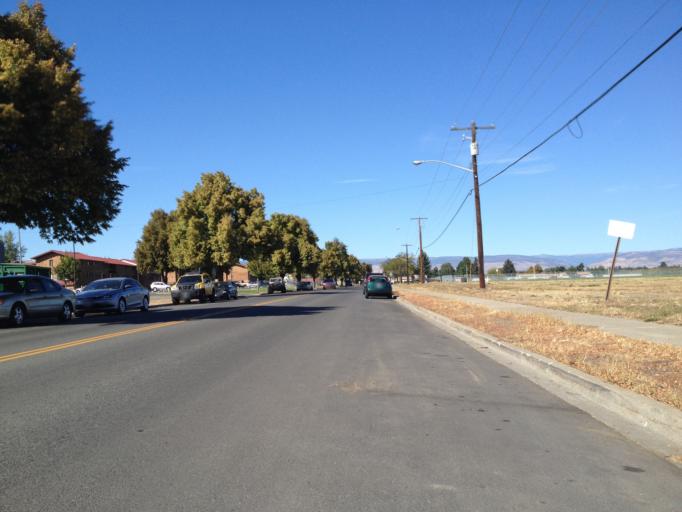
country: US
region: Washington
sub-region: Kittitas County
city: Ellensburg
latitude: 47.0068
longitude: -120.5319
